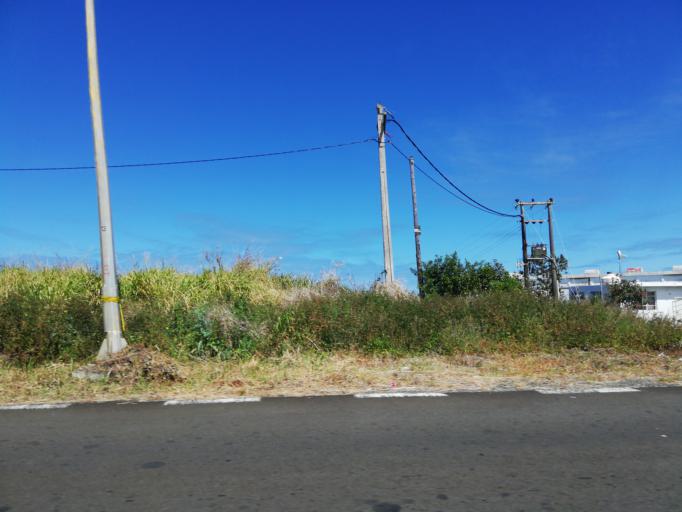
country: MU
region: Grand Port
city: Plaine Magnien
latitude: -20.4439
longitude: 57.6847
